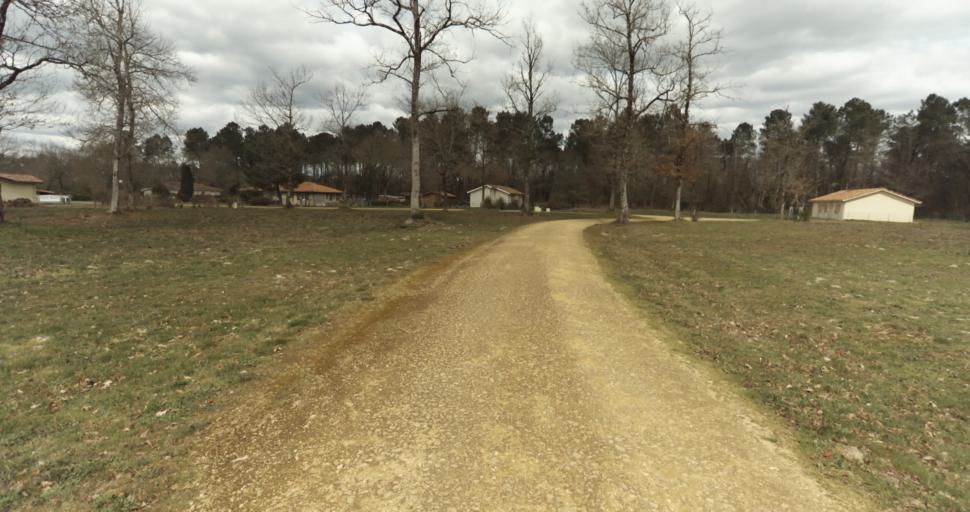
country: FR
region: Aquitaine
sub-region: Departement des Landes
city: Roquefort
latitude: 44.0711
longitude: -0.4257
